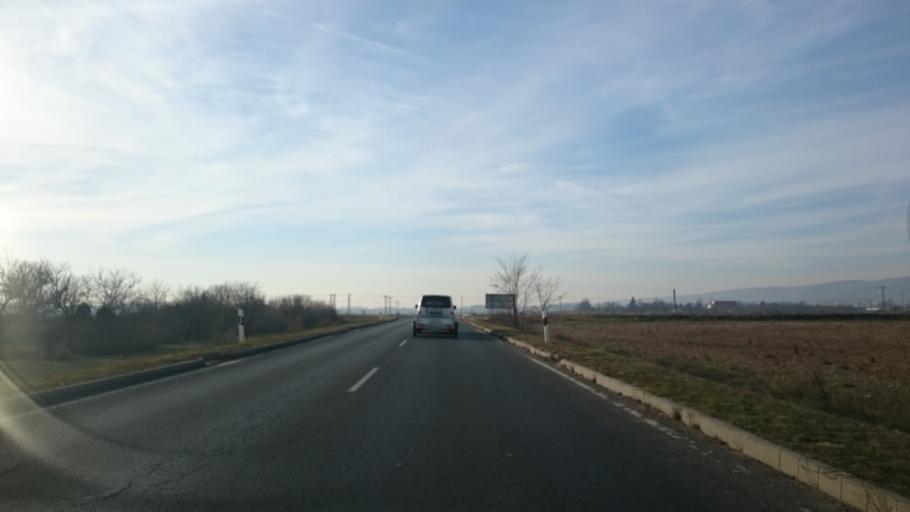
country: HU
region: Baranya
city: Pellerd
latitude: 46.0550
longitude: 18.1861
